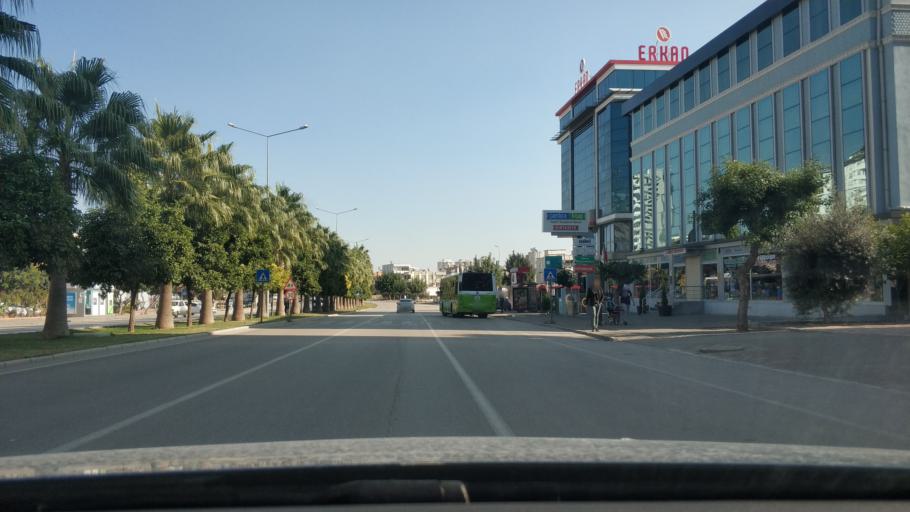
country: TR
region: Adana
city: Seyhan
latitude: 37.0206
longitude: 35.2688
